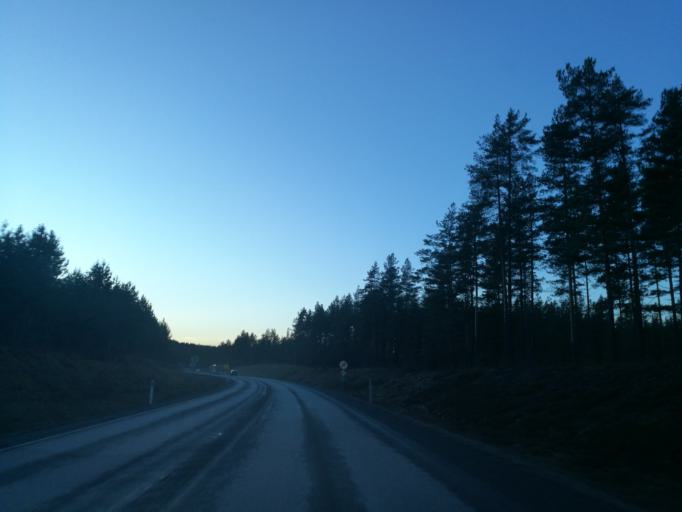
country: NO
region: Hedmark
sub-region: Eidskog
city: Skotterud
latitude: 59.9382
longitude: 12.2124
